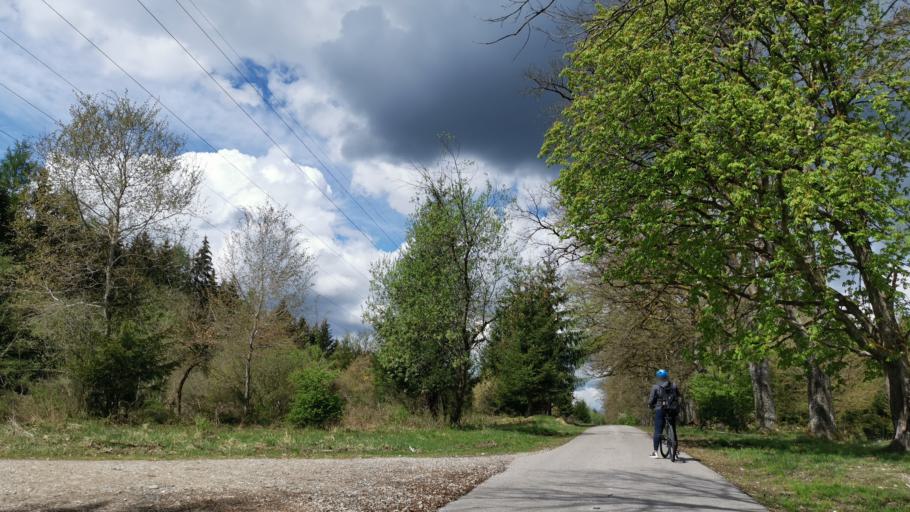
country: DE
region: Bavaria
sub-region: Upper Bavaria
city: Baierbrunn
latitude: 48.0487
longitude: 11.4691
